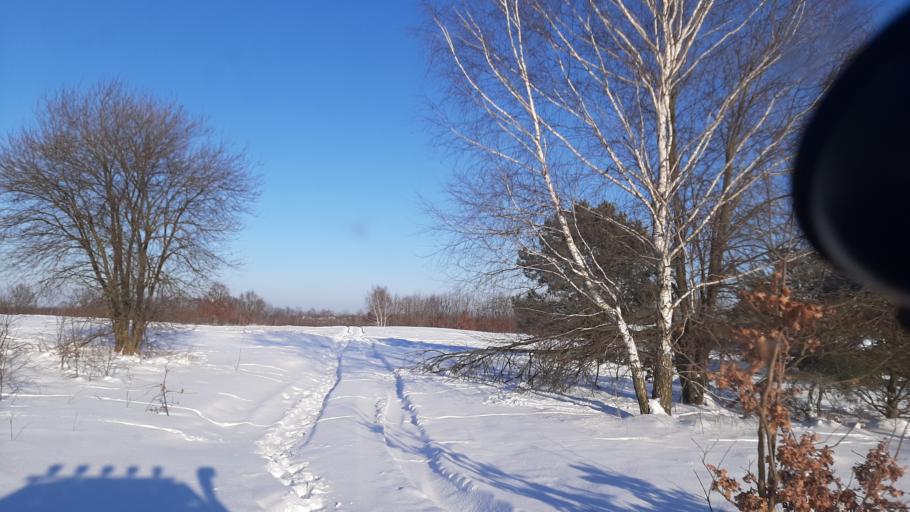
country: PL
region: Lublin Voivodeship
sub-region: Powiat lubelski
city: Jastkow
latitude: 51.3858
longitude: 22.4285
